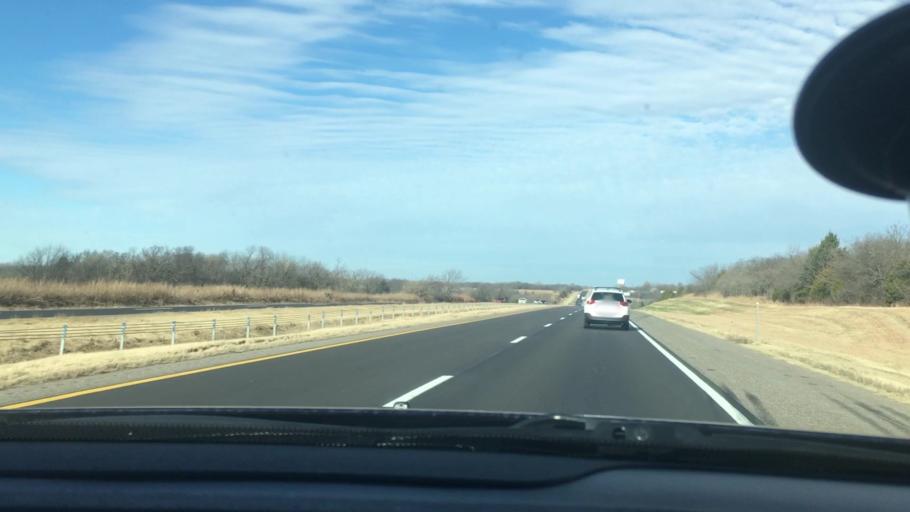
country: US
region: Oklahoma
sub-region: Cleveland County
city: Noble
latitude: 35.0979
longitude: -97.4255
